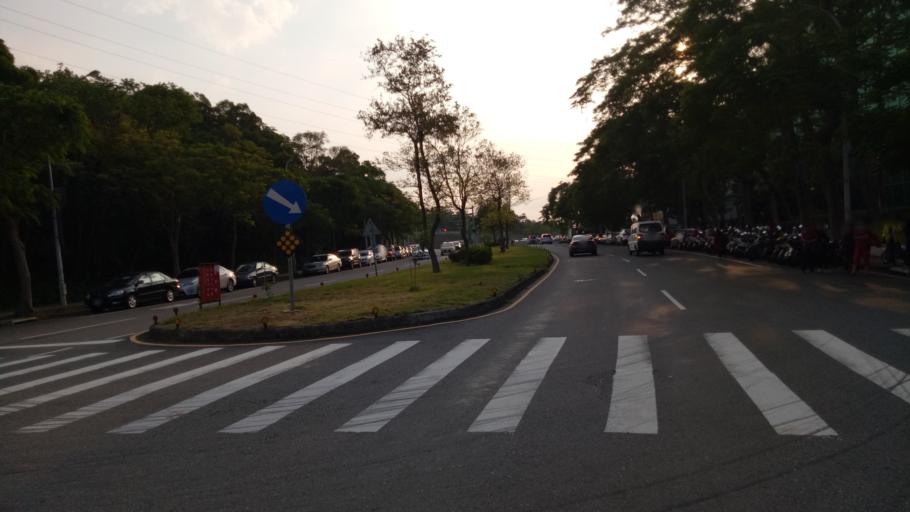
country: TW
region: Taiwan
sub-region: Hsinchu
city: Hsinchu
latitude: 24.7680
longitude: 121.0175
